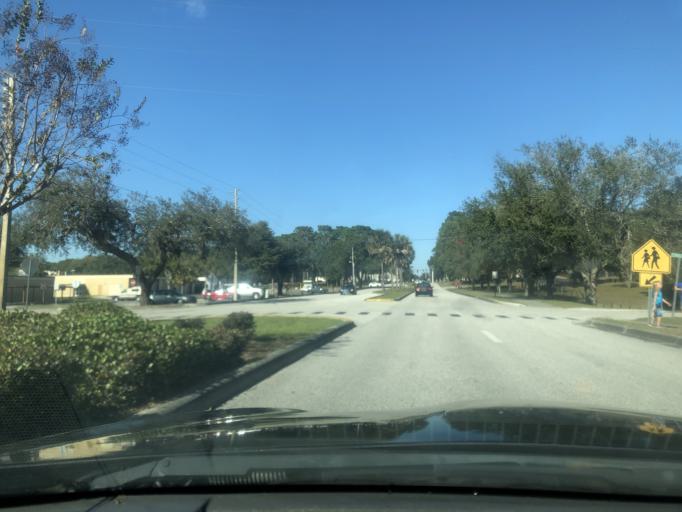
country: US
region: Florida
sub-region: Citrus County
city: Inverness
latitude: 28.8334
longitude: -82.3447
